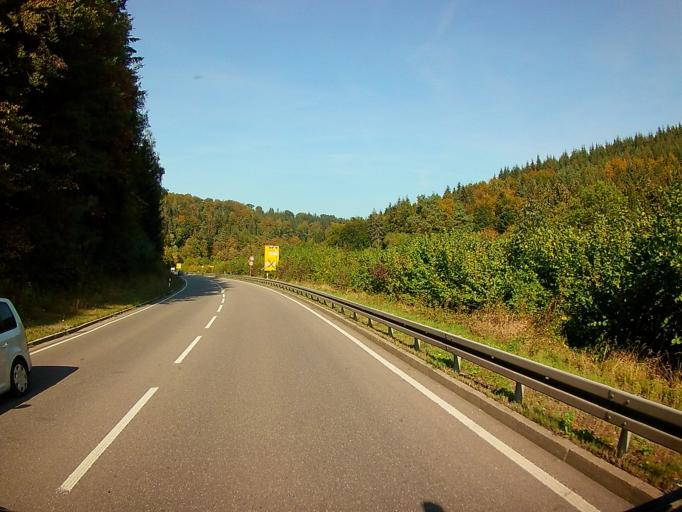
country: DE
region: Baden-Wuerttemberg
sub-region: Karlsruhe Region
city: Birkenfeld
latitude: 48.8598
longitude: 8.6385
